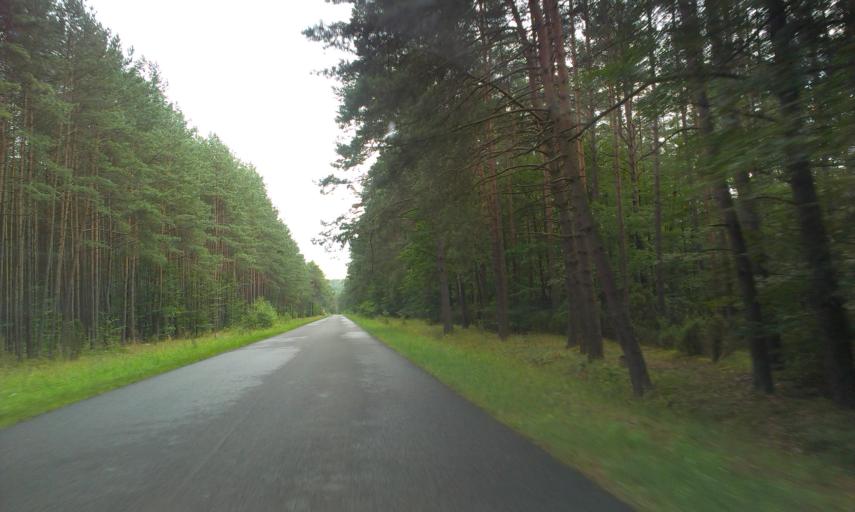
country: PL
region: Greater Poland Voivodeship
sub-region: Powiat zlotowski
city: Okonek
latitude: 53.4993
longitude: 16.9810
